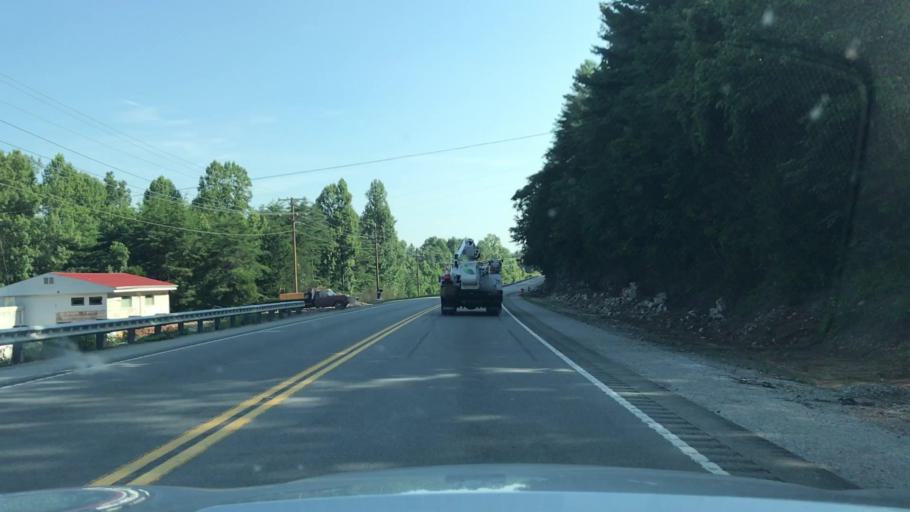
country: US
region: Tennessee
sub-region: Overton County
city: Livingston
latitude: 36.4293
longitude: -85.2804
